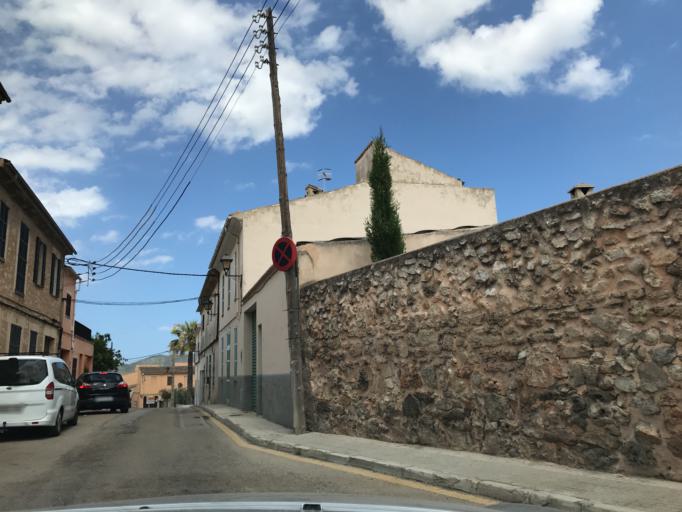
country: ES
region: Balearic Islands
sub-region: Illes Balears
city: Son Servera
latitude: 39.6234
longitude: 3.3578
